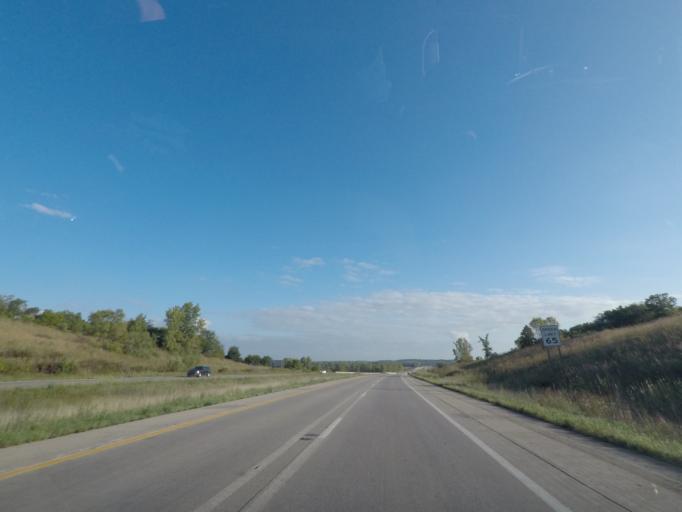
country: US
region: Iowa
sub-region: Warren County
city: Carlisle
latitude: 41.5354
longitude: -93.5183
